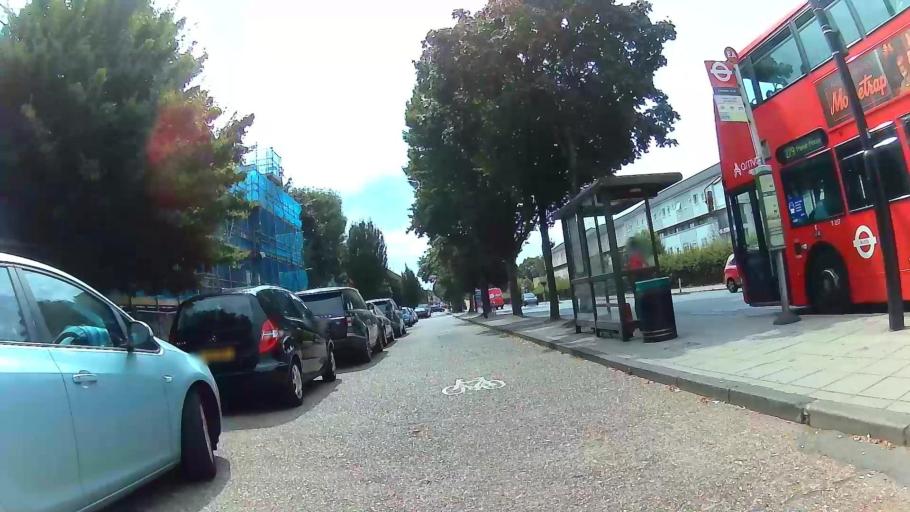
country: GB
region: England
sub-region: Hertfordshire
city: Waltham Cross
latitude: 51.6620
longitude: -0.0457
